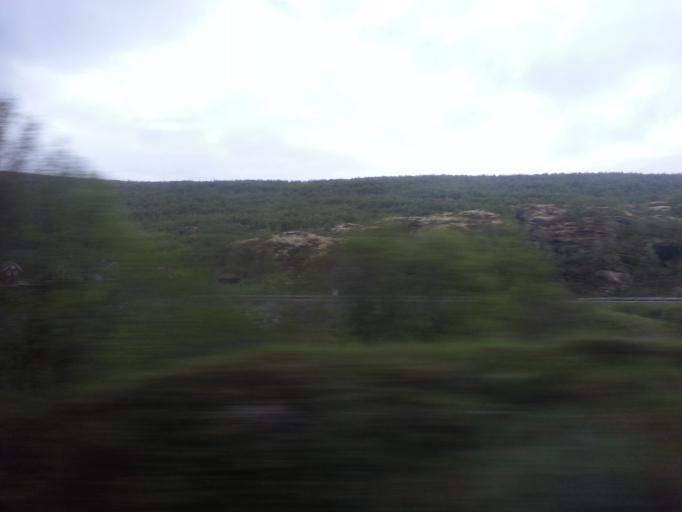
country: NO
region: Sor-Trondelag
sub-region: Oppdal
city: Oppdal
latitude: 62.3022
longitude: 9.6016
